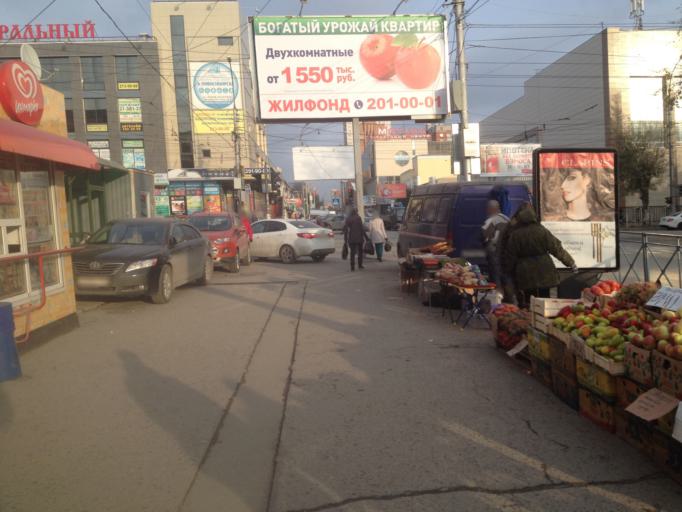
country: RU
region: Novosibirsk
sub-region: Novosibirskiy Rayon
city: Novosibirsk
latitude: 55.0407
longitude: 82.9211
